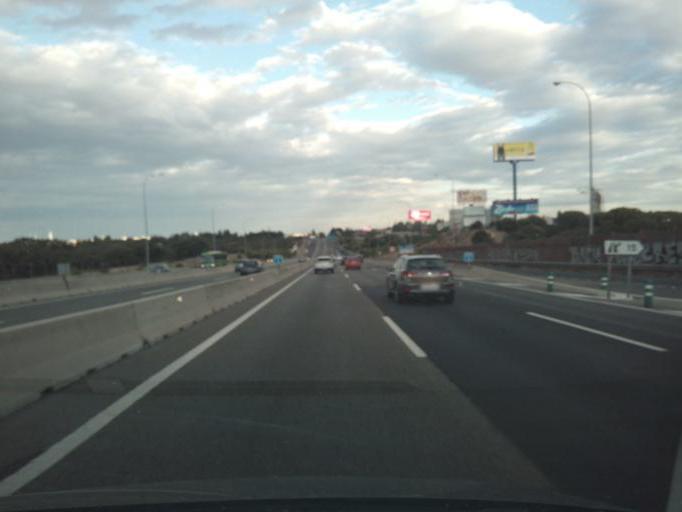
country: ES
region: Madrid
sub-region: Provincia de Madrid
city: Majadahonda
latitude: 40.4796
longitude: -3.8491
